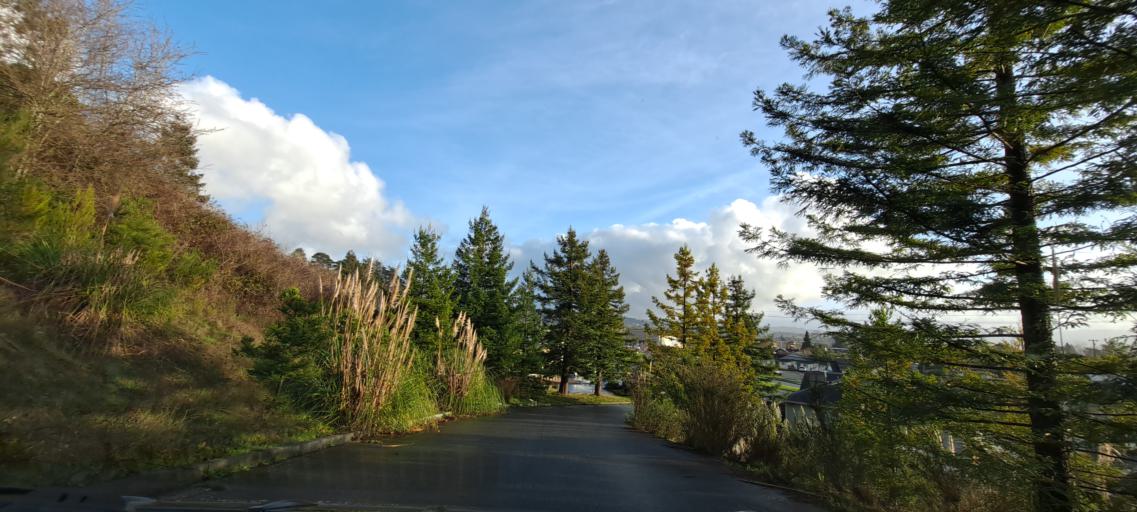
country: US
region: California
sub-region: Humboldt County
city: Fortuna
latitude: 40.5982
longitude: -124.1477
